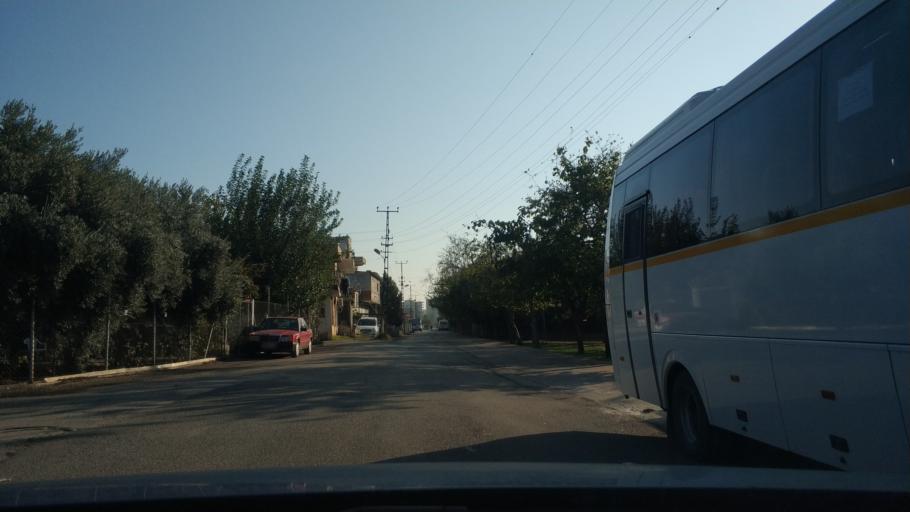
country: TR
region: Adana
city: Seyhan
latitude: 37.0117
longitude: 35.2948
